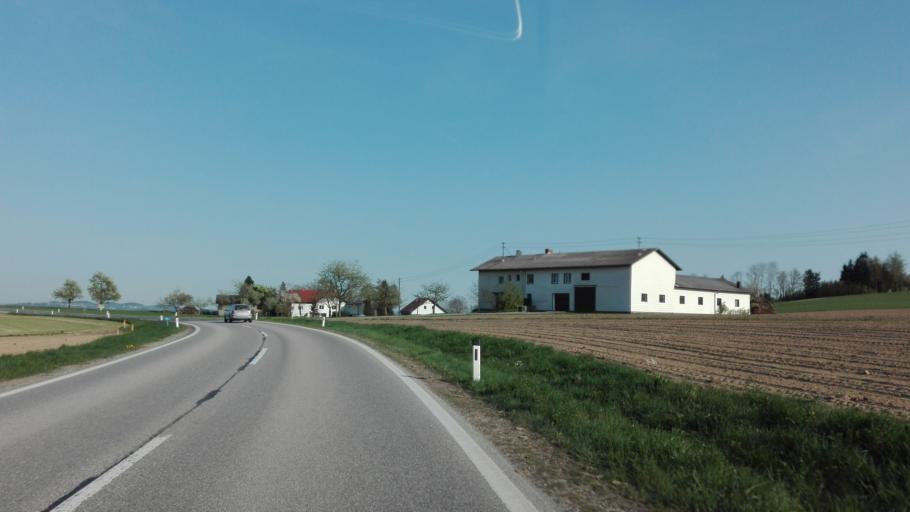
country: AT
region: Upper Austria
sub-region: Politischer Bezirk Grieskirchen
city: Grieskirchen
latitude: 48.3442
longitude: 13.7891
